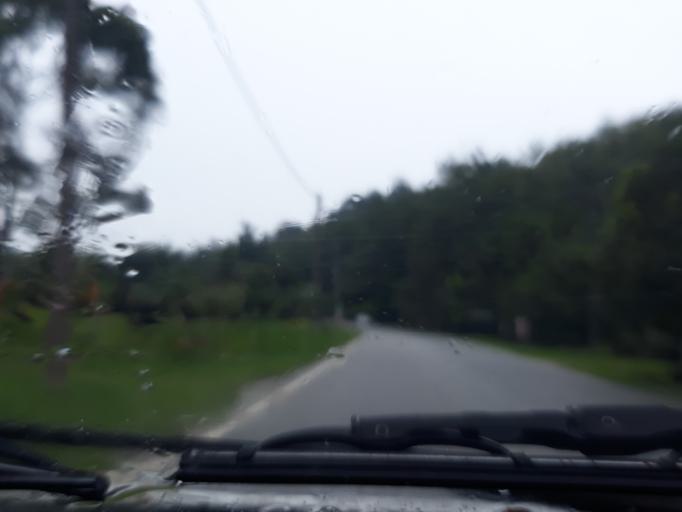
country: MY
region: Kedah
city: Kulim
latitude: 5.2750
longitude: 100.6168
